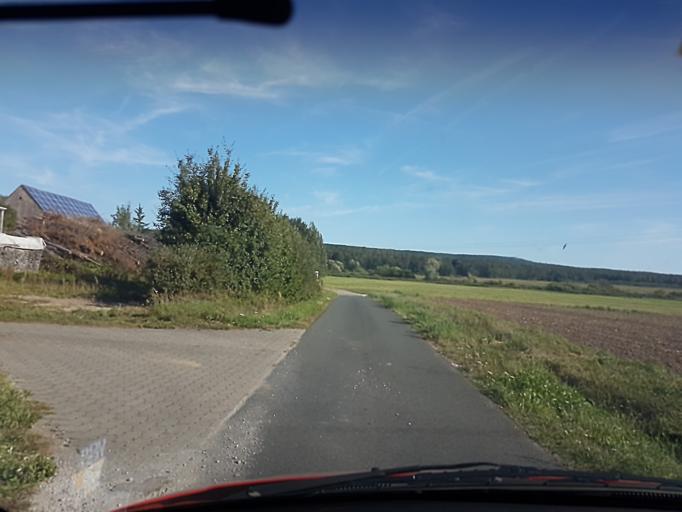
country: DE
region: Bavaria
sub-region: Upper Franconia
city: Hallerndorf
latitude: 49.7324
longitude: 10.9394
